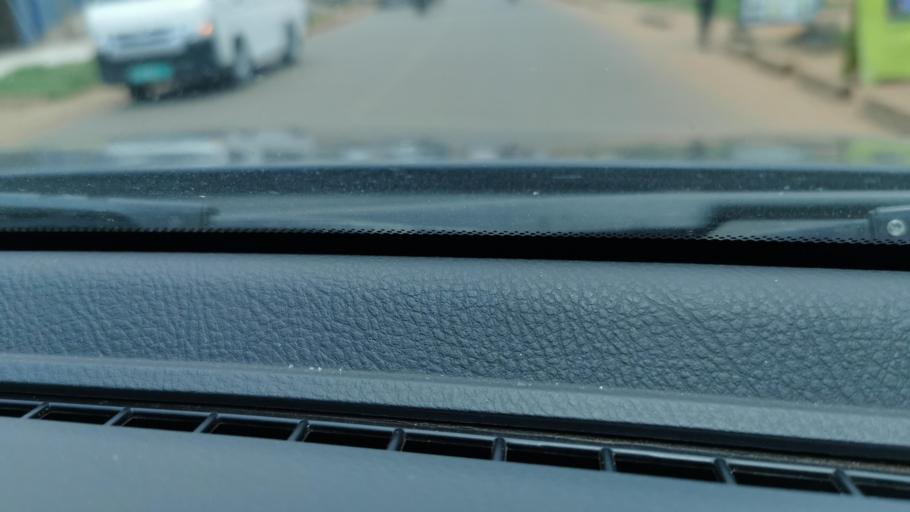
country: TG
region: Maritime
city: Lome
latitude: 6.2191
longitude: 1.1982
